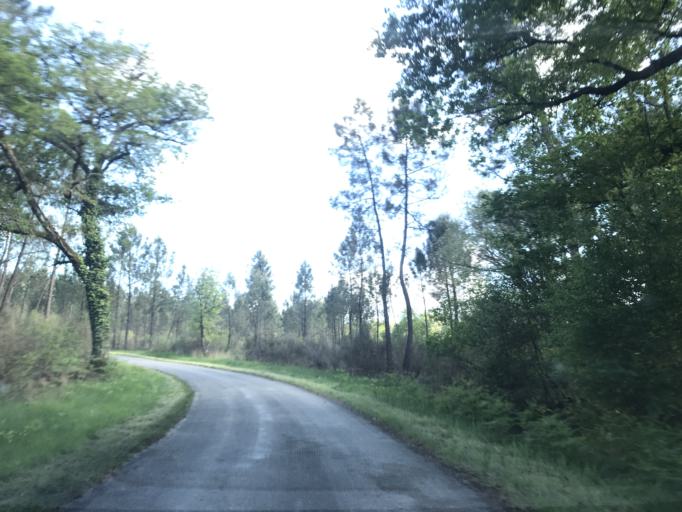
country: FR
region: Poitou-Charentes
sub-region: Departement de la Charente
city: Chalais
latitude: 45.2814
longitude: -0.0593
